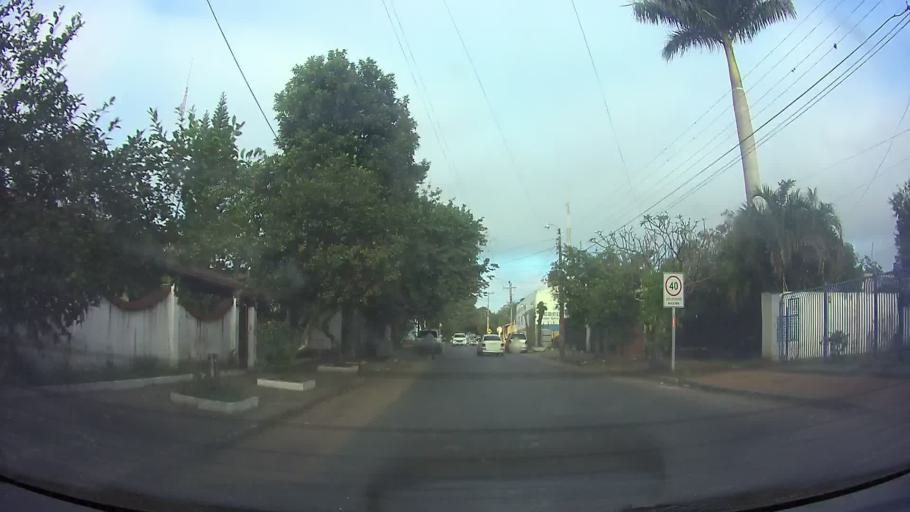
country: PY
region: Central
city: Villa Elisa
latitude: -25.3377
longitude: -57.5639
